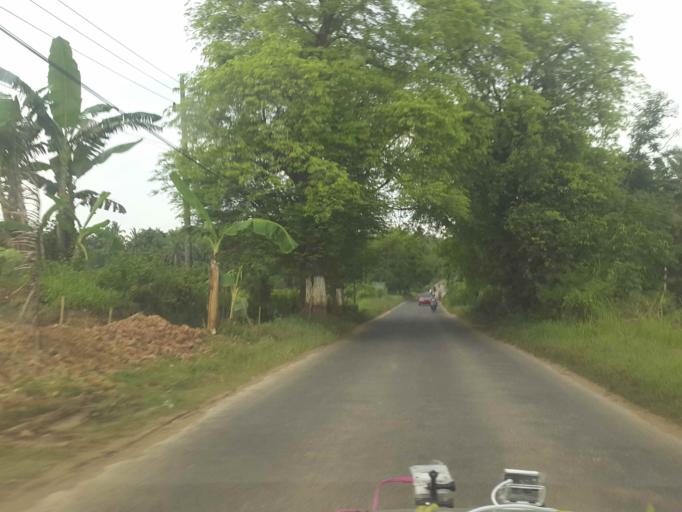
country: ID
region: East Java
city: Ganjur
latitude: -6.9728
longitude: 113.8623
